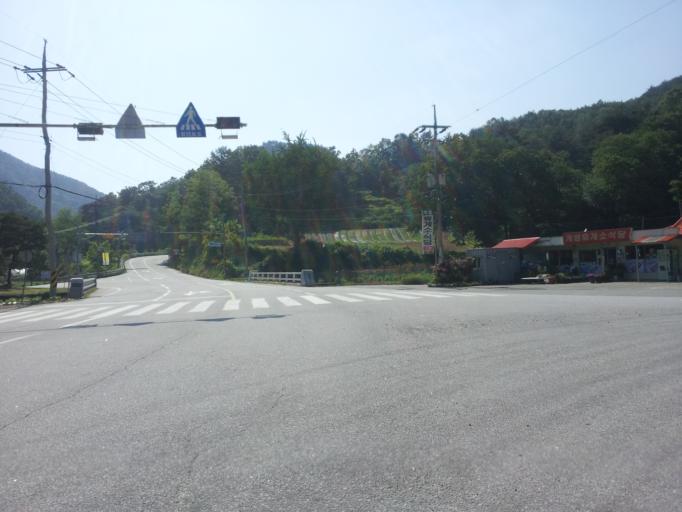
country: KR
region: Chungcheongbuk-do
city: Okcheon
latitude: 36.4791
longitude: 127.6560
